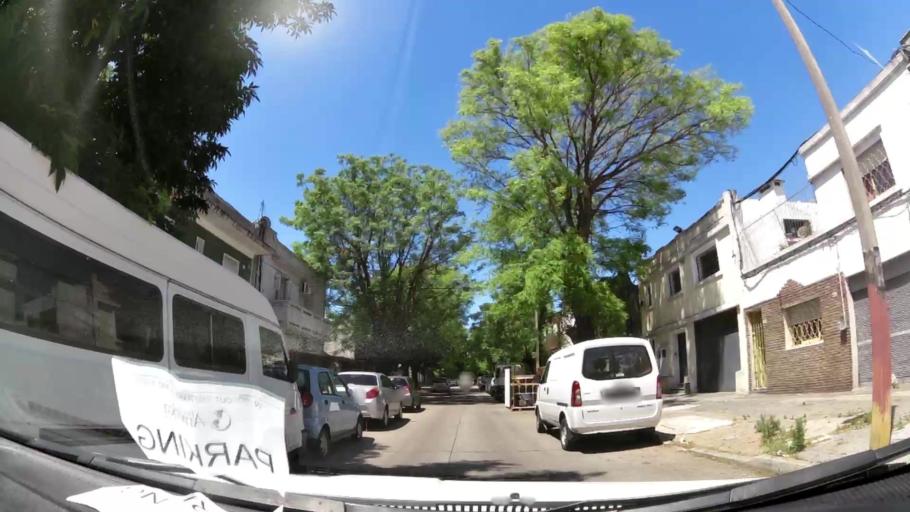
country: UY
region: Montevideo
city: Montevideo
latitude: -34.8848
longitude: -56.1713
